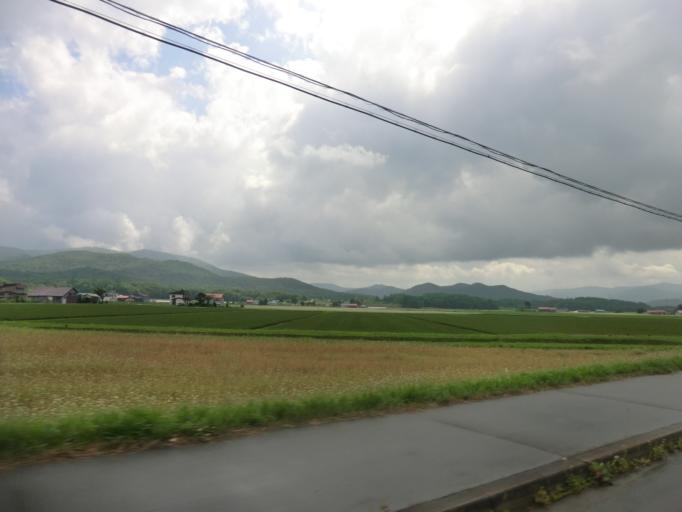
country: JP
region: Hokkaido
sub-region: Asahikawa-shi
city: Asahikawa
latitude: 44.0250
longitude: 142.1522
